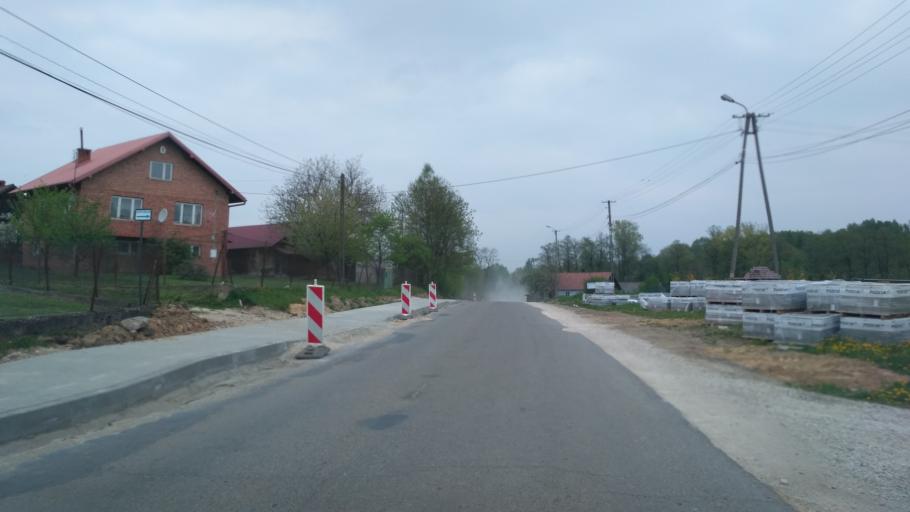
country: PL
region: Lesser Poland Voivodeship
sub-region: Powiat tarnowski
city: Skrzyszow
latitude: 49.9801
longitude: 21.0652
